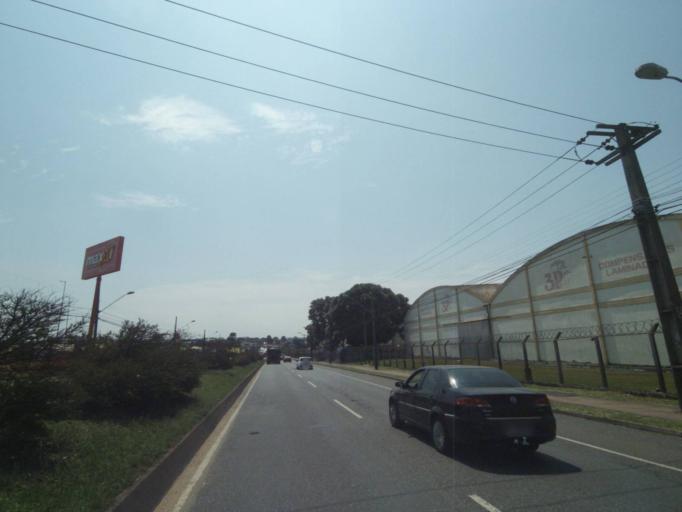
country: BR
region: Parana
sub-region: Curitiba
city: Curitiba
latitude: -25.4844
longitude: -49.3175
